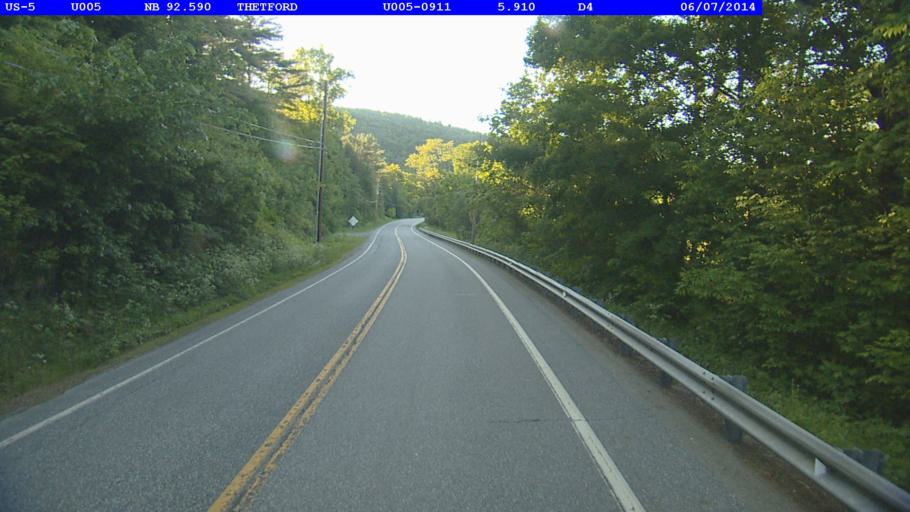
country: US
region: New Hampshire
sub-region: Grafton County
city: Lyme
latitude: 43.8511
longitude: -72.1871
